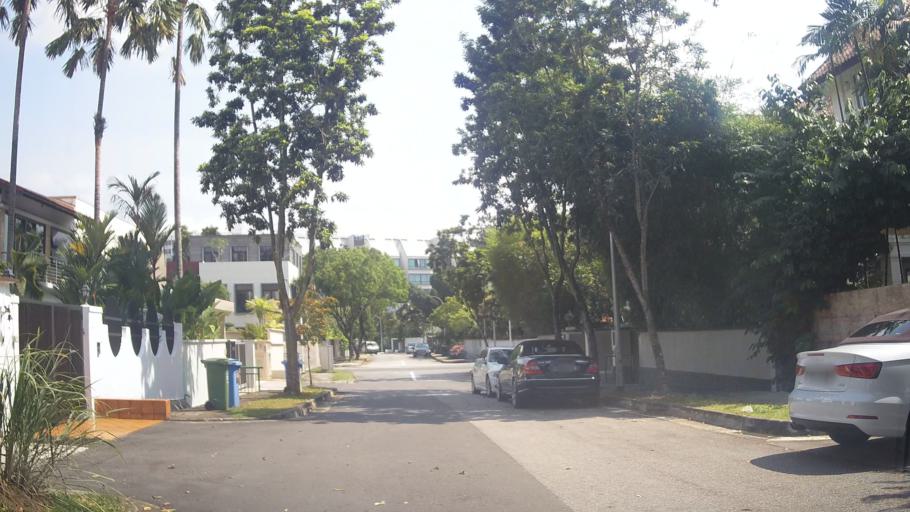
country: SG
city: Singapore
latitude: 1.3221
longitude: 103.8009
